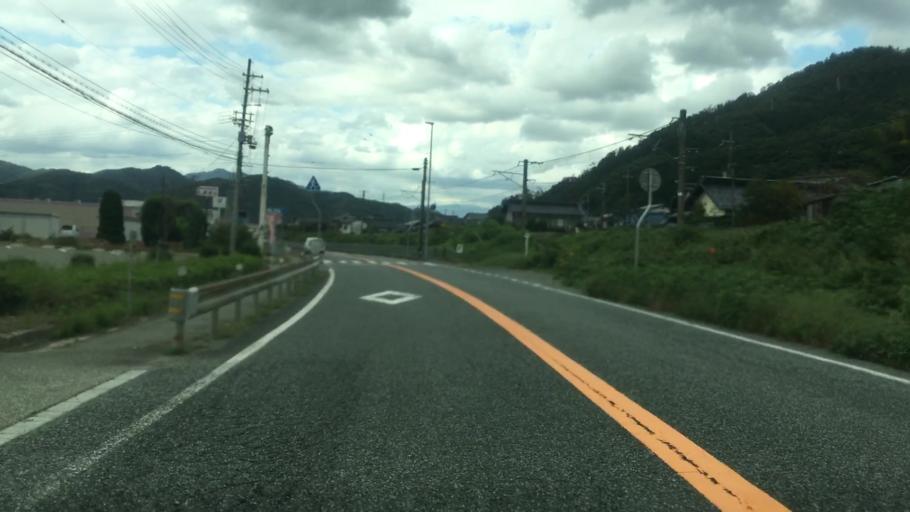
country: JP
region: Hyogo
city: Toyooka
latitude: 35.3259
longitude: 134.8758
